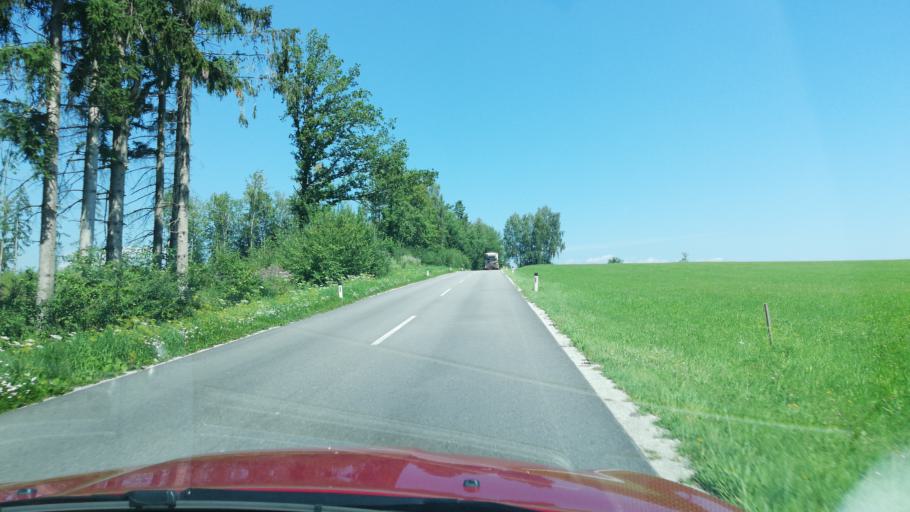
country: AT
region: Upper Austria
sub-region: Politischer Bezirk Rohrbach
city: Kleinzell im Muehlkreis
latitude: 48.4598
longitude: 14.0510
